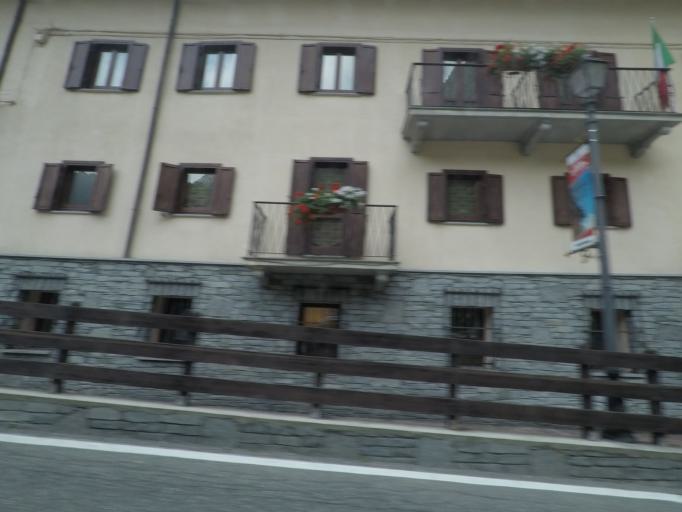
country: IT
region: Aosta Valley
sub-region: Valle d'Aosta
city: Antey-Saint-Andre
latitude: 45.8238
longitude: 7.5917
